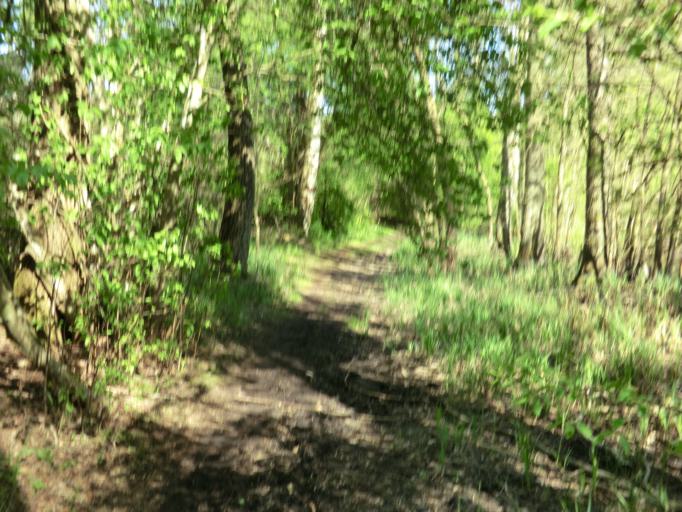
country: SE
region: Skane
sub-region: Sjobo Kommun
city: Sjoebo
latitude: 55.5745
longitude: 13.7181
